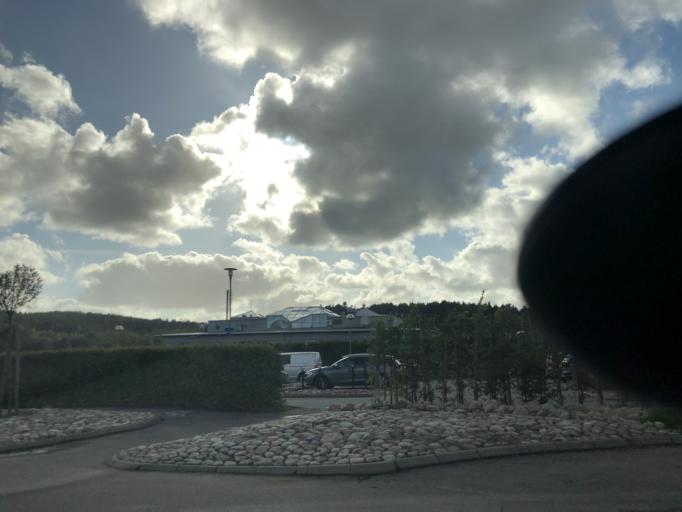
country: SE
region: Vaestra Goetaland
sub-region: Goteborg
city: Goeteborg
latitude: 57.7459
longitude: 11.9448
